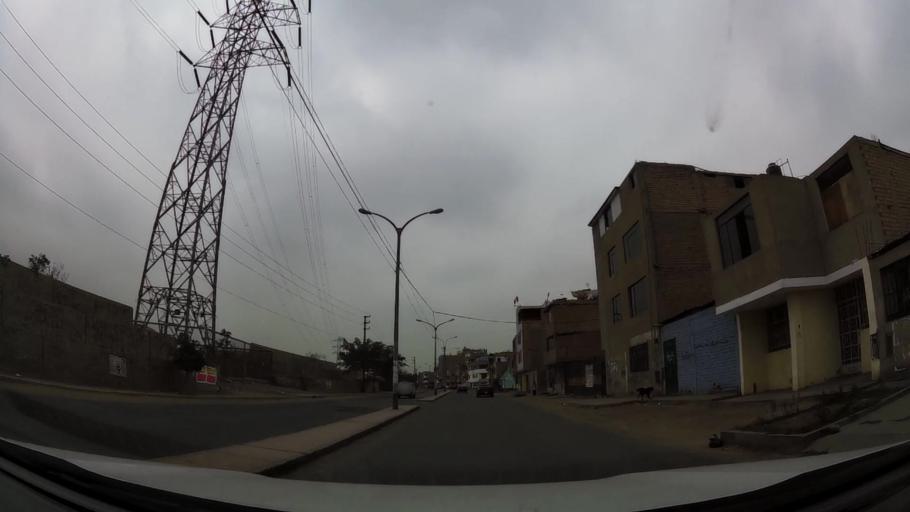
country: PE
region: Lima
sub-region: Lima
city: Independencia
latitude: -11.9420
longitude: -77.0877
